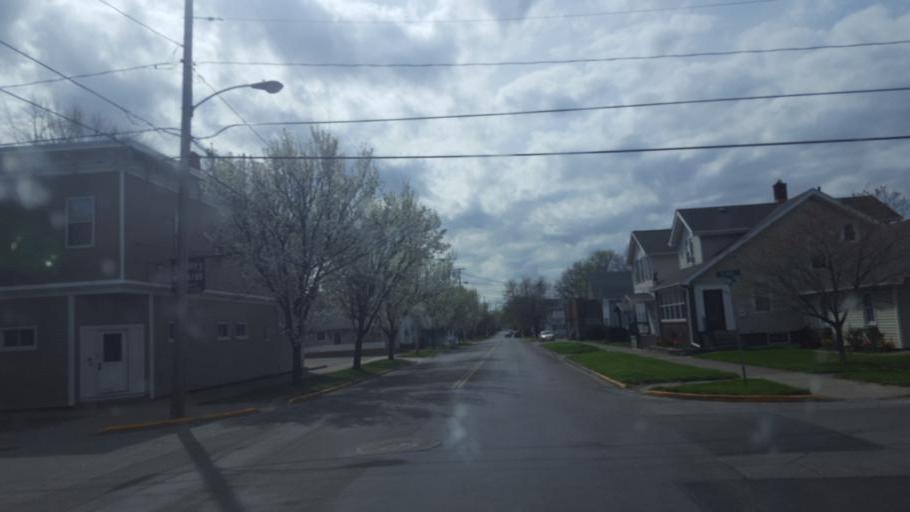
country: US
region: Ohio
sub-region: Erie County
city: Sandusky
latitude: 41.4467
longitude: -82.7216
